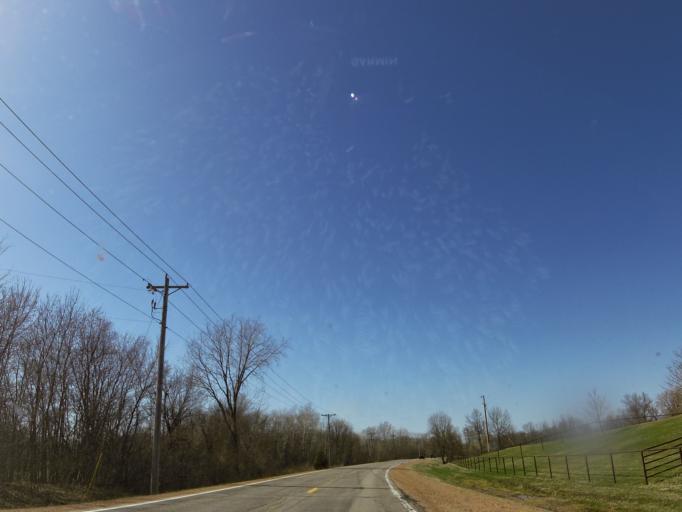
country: US
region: Minnesota
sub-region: Dakota County
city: Lakeville
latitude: 44.6580
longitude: -93.3315
